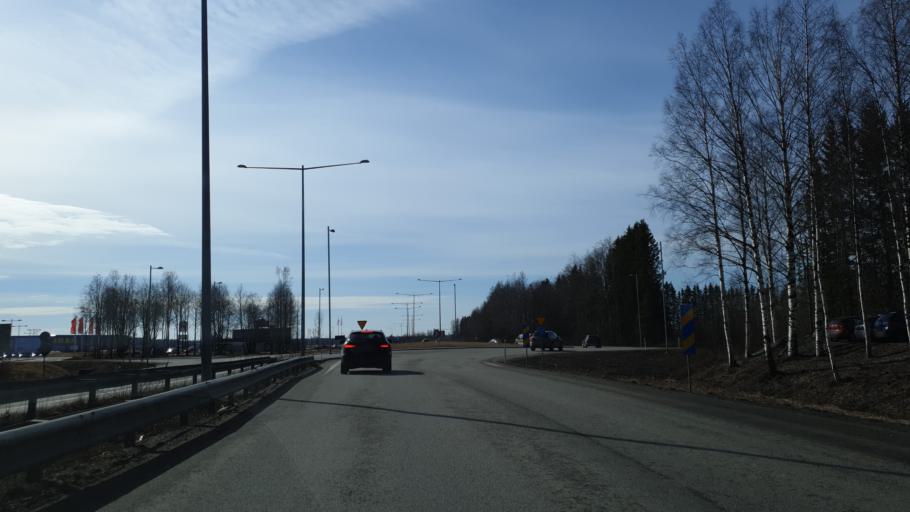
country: SE
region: Vaesterbotten
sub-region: Umea Kommun
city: Umea
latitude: 63.8126
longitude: 20.2492
